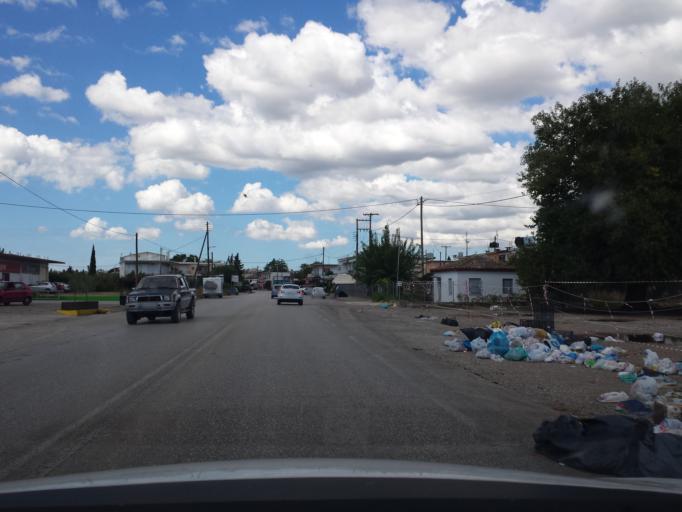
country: GR
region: West Greece
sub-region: Nomos Ileias
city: Pyrgos
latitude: 37.6638
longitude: 21.4591
